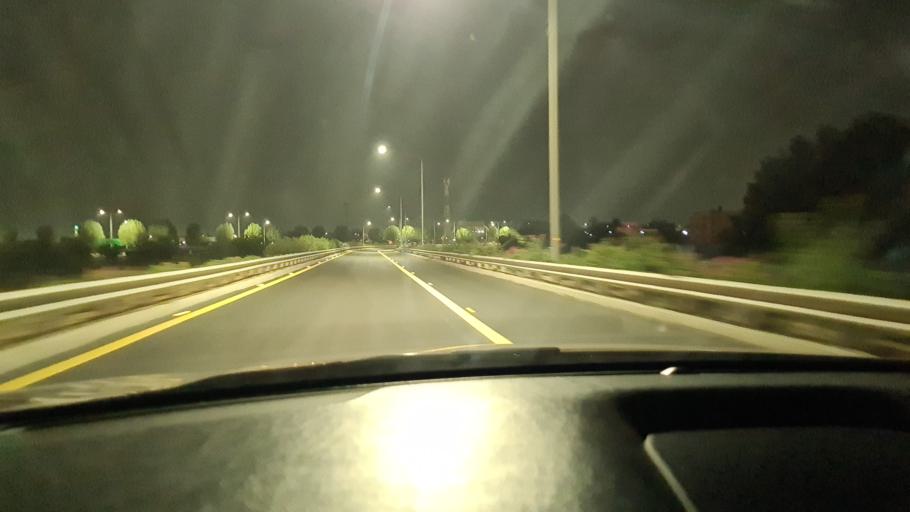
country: SA
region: Eastern Province
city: Al Jubayl
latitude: 27.1212
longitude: 49.5418
